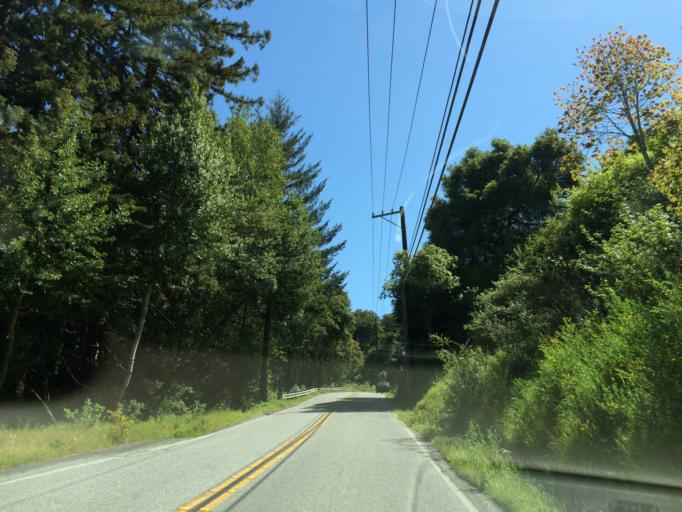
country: US
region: California
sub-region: Santa Clara County
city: Lexington Hills
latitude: 37.1819
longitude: -122.0033
